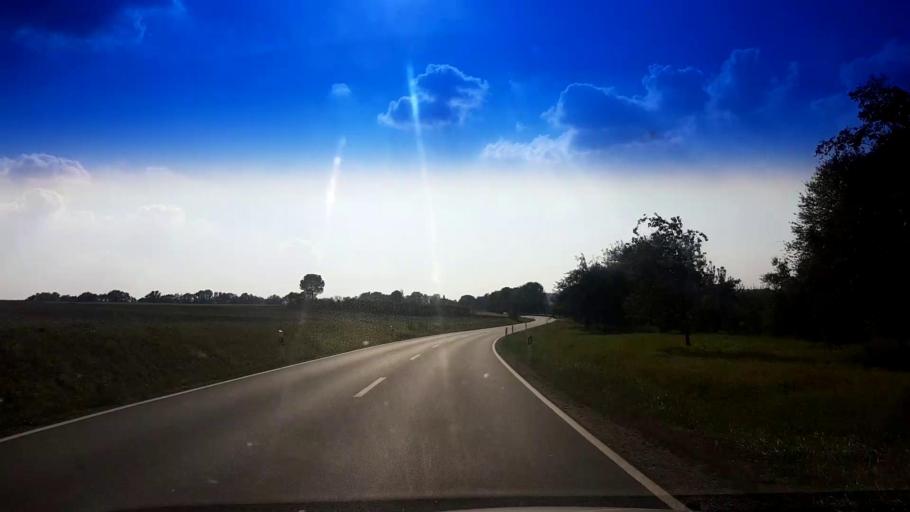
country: DE
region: Bavaria
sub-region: Upper Franconia
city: Schesslitz
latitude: 49.9618
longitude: 11.0105
